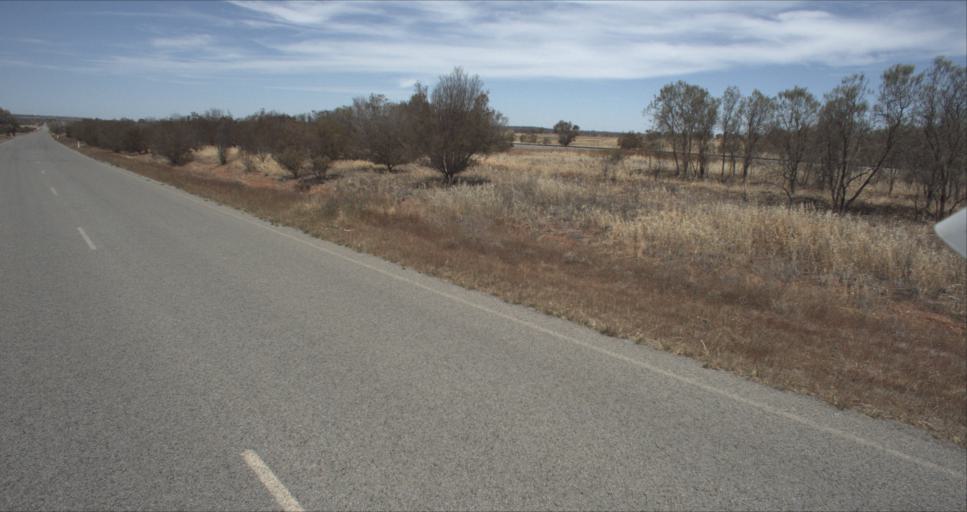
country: AU
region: New South Wales
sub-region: Leeton
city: Leeton
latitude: -34.6211
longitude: 146.4464
